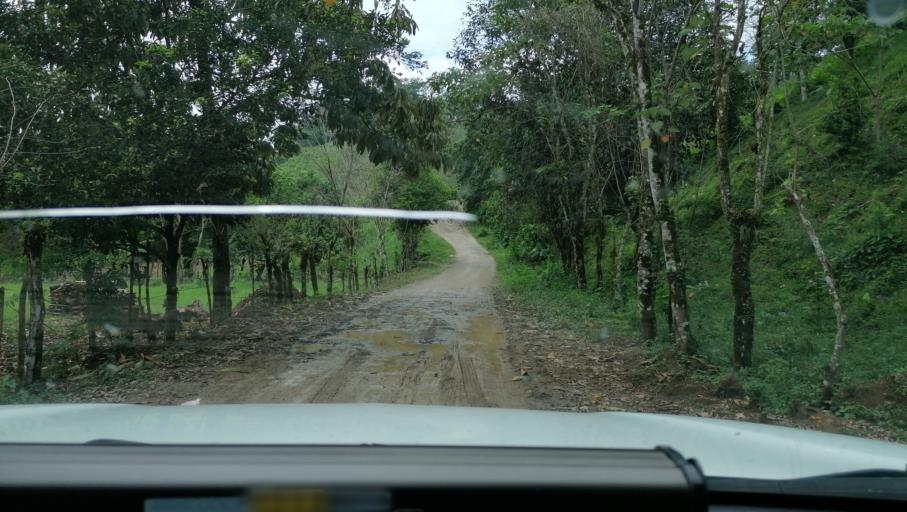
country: MX
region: Chiapas
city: Ocotepec
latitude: 17.3192
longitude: -93.1378
